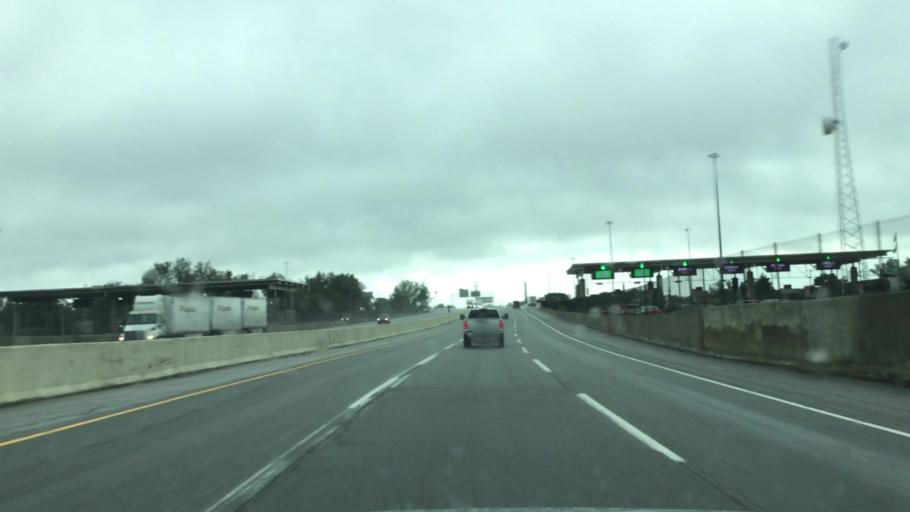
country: US
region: Indiana
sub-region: Lake County
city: Gary
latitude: 41.5908
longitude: -87.3046
